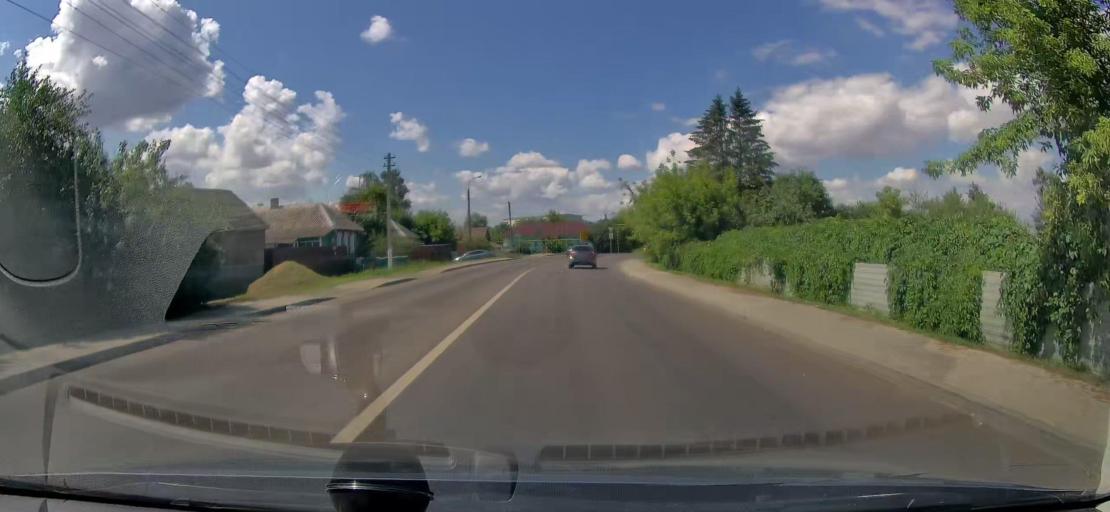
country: RU
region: Kursk
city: Zolotukhino
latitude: 51.9722
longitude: 36.2981
